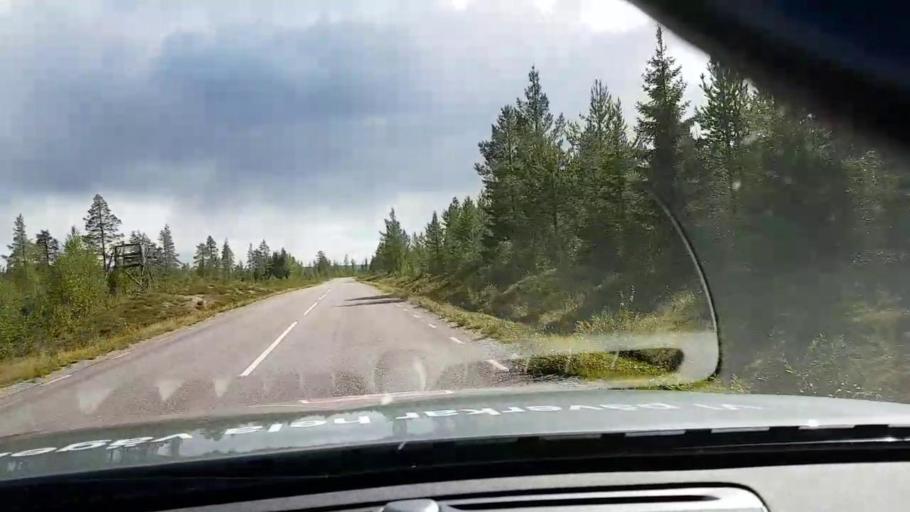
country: SE
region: Vaesterbotten
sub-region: Asele Kommun
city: Asele
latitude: 63.8992
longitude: 17.3488
